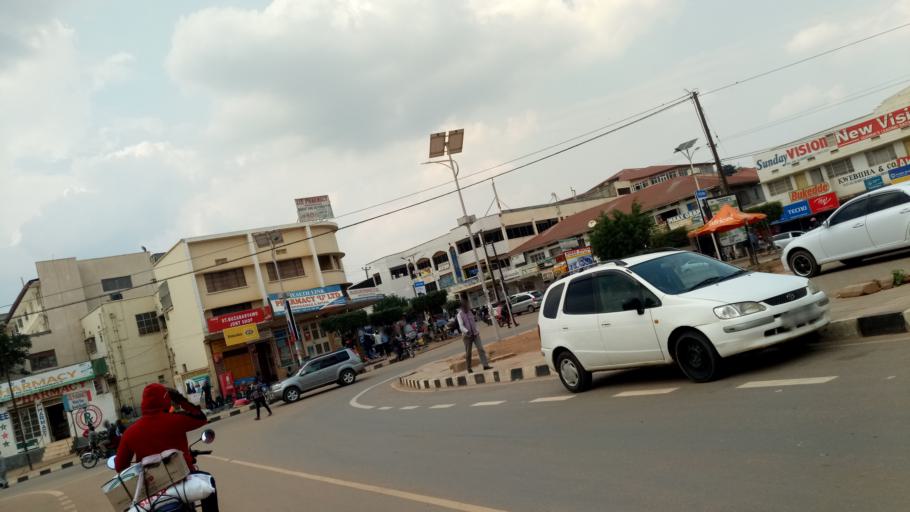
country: UG
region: Western Region
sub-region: Mbarara District
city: Mbarara
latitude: -0.6080
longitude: 30.6605
